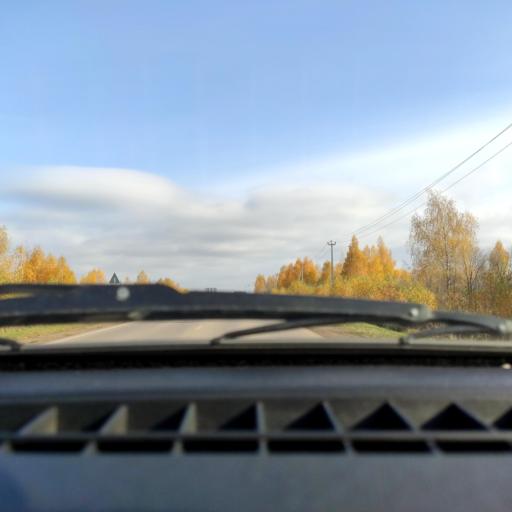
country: RU
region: Bashkortostan
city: Kabakovo
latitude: 54.6978
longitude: 56.1551
